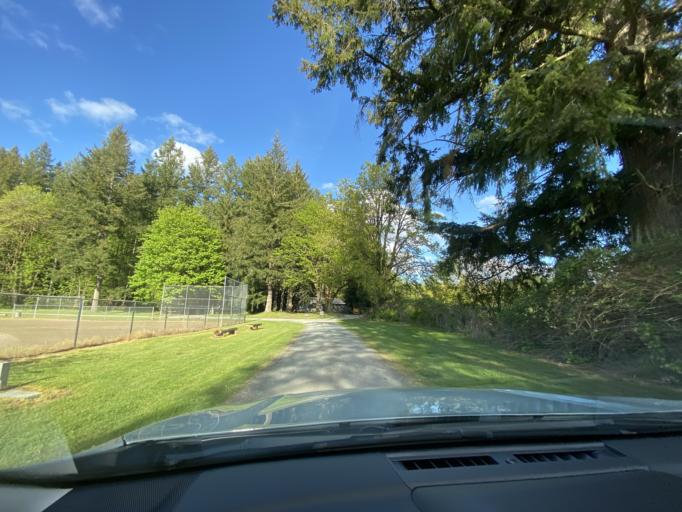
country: US
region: Washington
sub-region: Pierce County
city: DuPont
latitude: 47.0469
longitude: -122.6904
